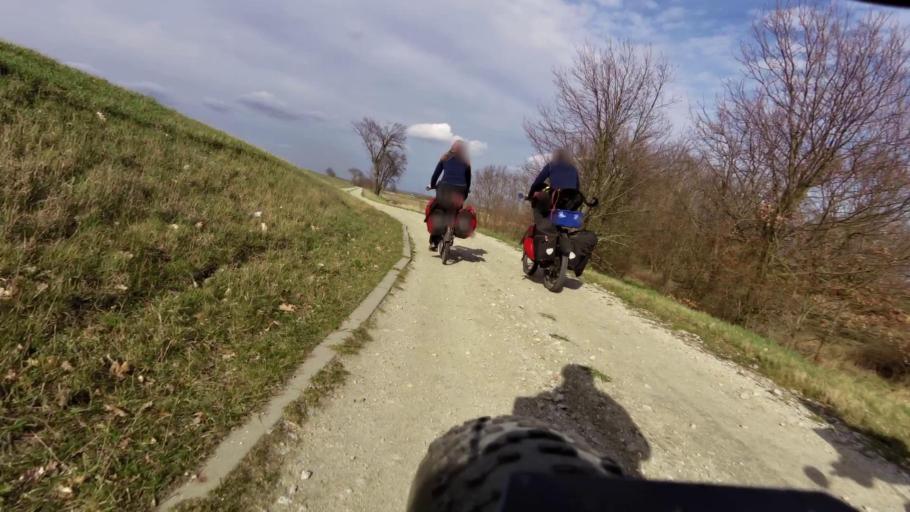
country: DE
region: Brandenburg
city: Reitwein
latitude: 52.5419
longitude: 14.6176
